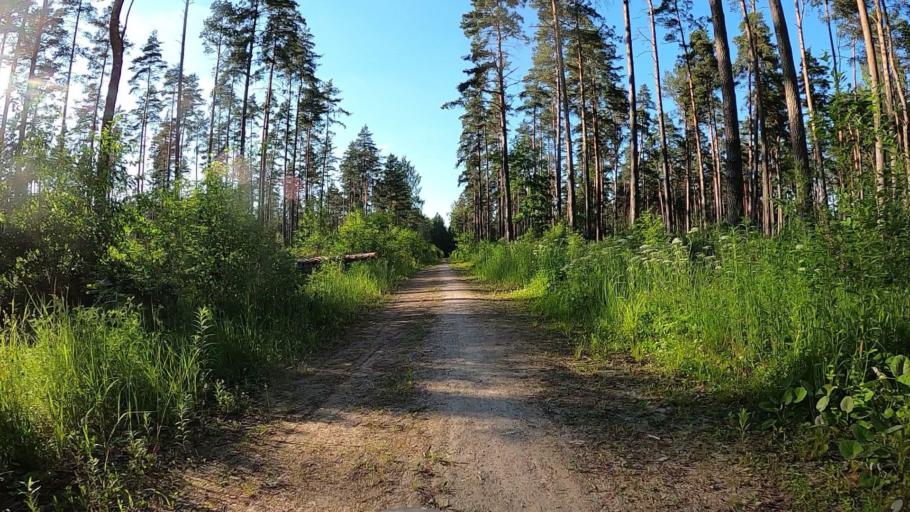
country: LV
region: Stopini
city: Ulbroka
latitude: 56.9251
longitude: 24.2351
